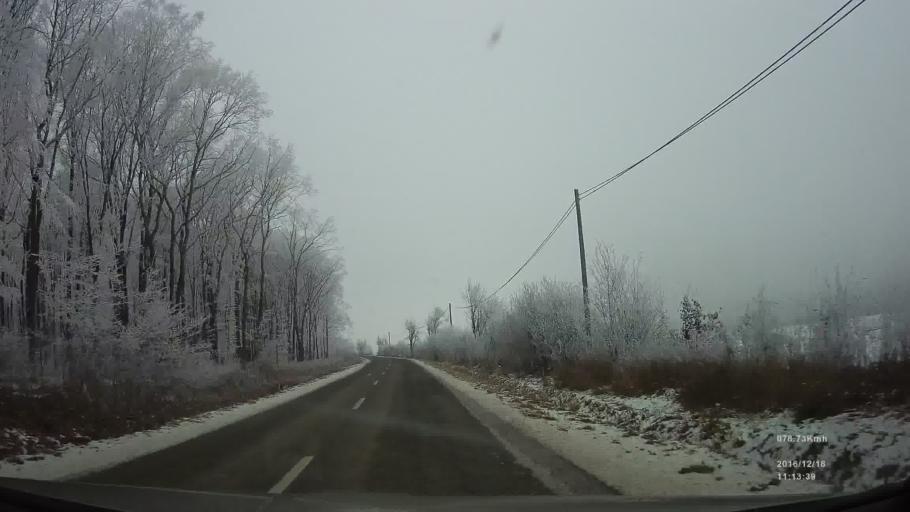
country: SK
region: Presovsky
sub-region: Okres Presov
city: Presov
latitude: 48.8847
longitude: 21.3136
